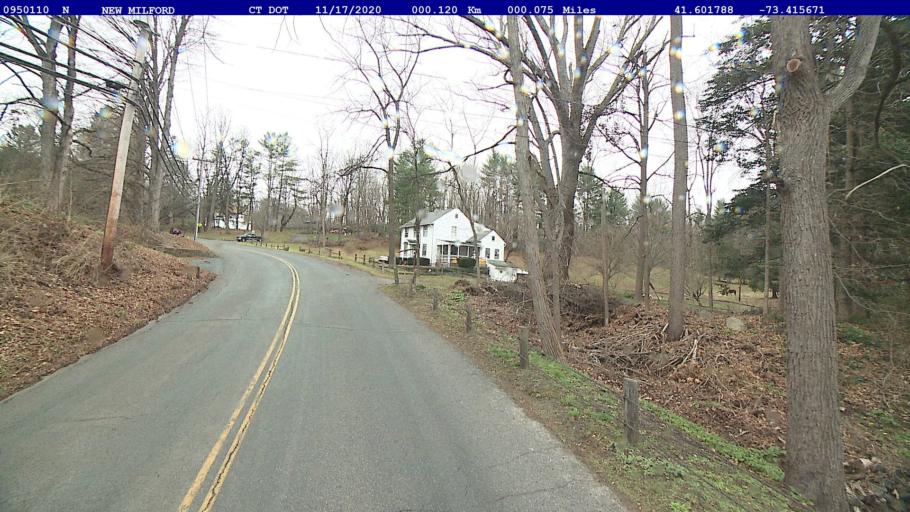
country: US
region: Connecticut
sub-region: Litchfield County
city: New Milford
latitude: 41.6018
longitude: -73.4157
